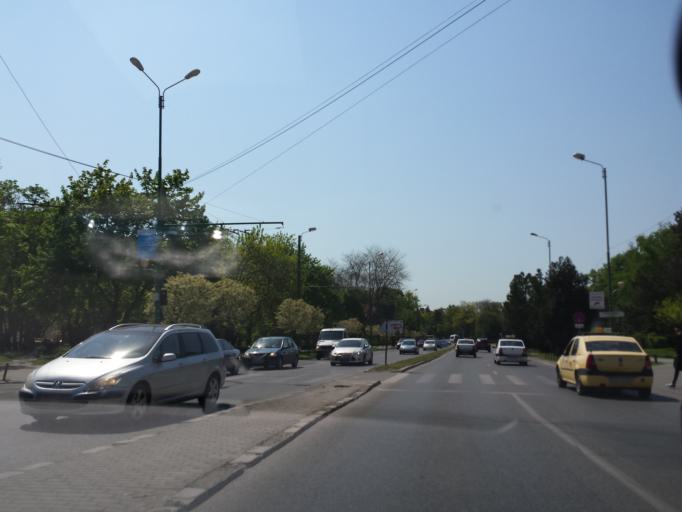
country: RO
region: Timis
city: Timisoara
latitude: 45.7550
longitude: 21.2332
